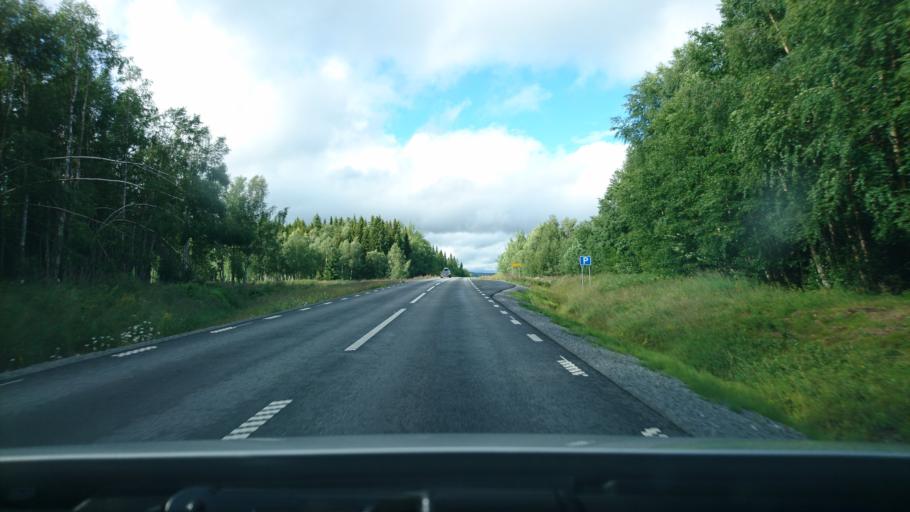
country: SE
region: Vaesterbotten
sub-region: Vilhelmina Kommun
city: Vilhelmina
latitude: 64.7146
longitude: 16.7064
